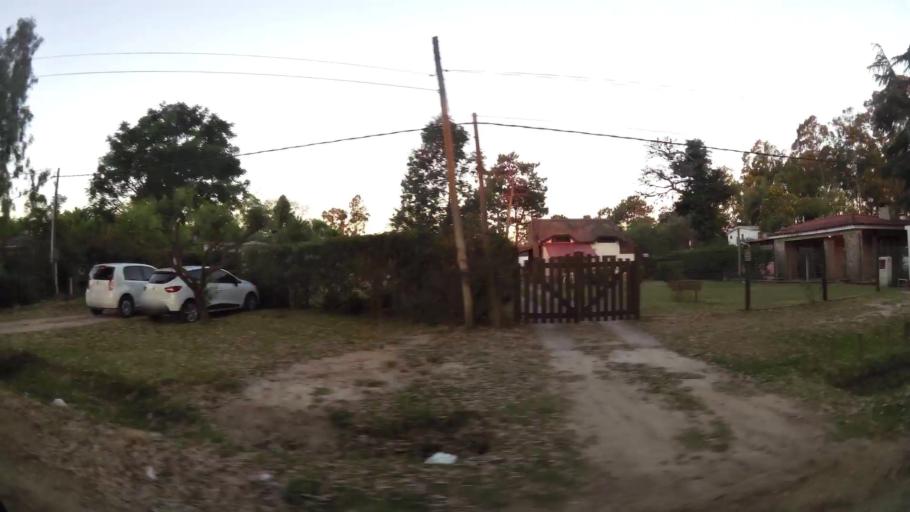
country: UY
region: Canelones
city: Barra de Carrasco
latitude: -34.8290
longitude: -55.9617
